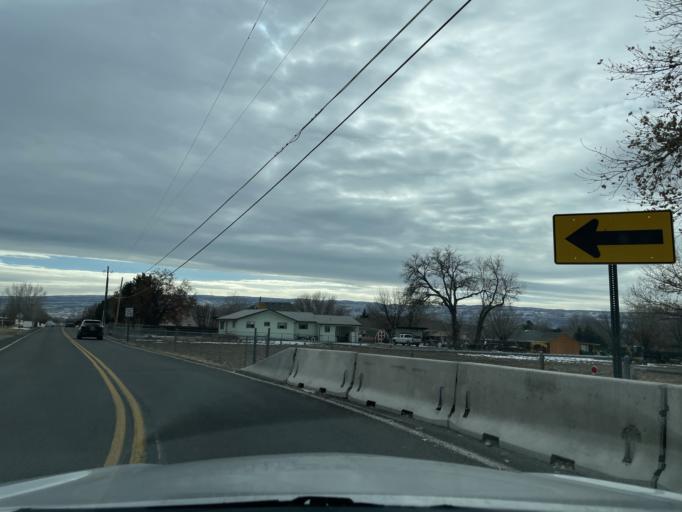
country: US
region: Colorado
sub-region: Mesa County
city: Grand Junction
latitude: 39.1055
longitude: -108.5800
